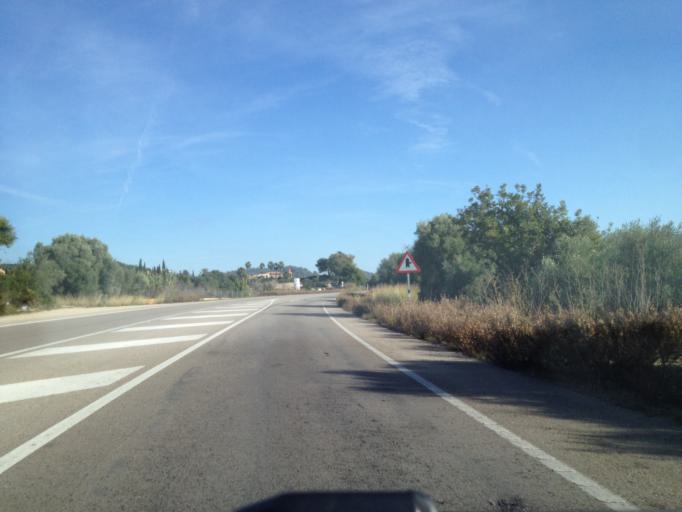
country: ES
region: Balearic Islands
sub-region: Illes Balears
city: Son Servera
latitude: 39.6428
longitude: 3.3735
